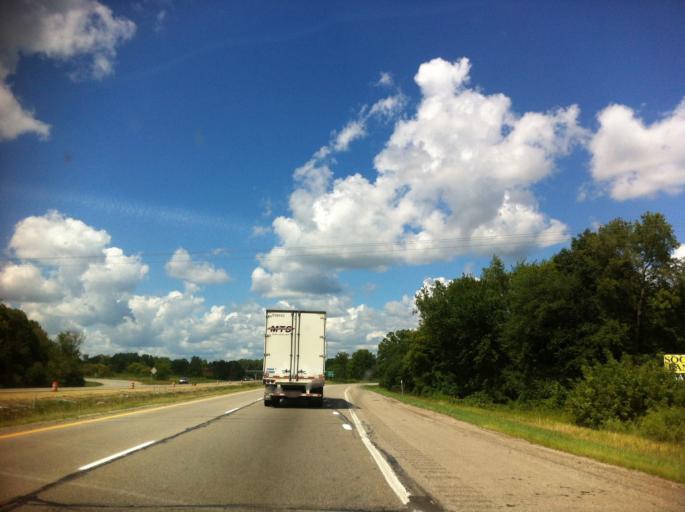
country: US
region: Michigan
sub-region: Washtenaw County
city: Ypsilanti
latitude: 42.2009
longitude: -83.6847
